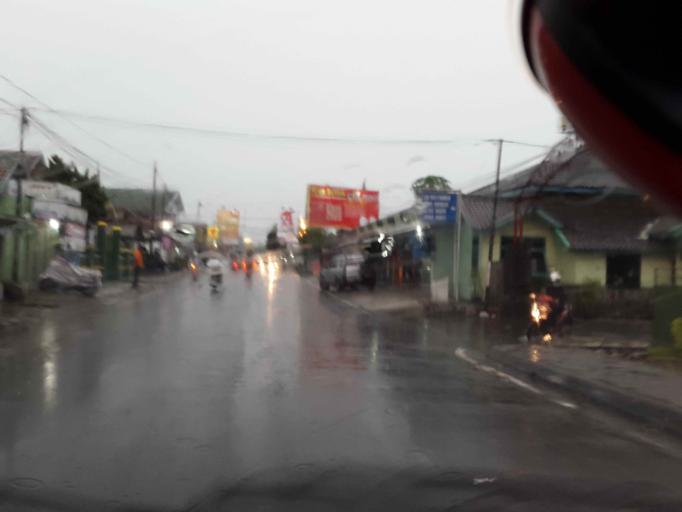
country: ID
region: West Java
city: Cimahi
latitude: -6.9168
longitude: 107.4921
